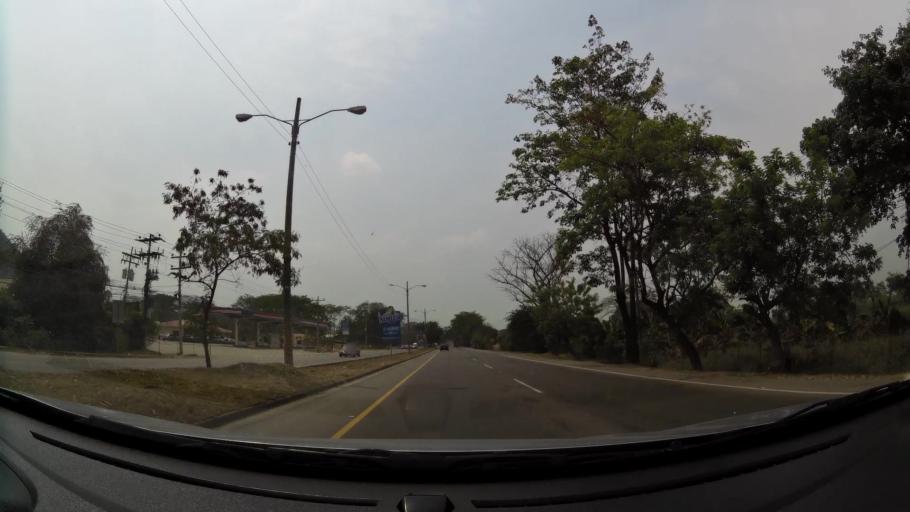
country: HN
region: Cortes
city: Nuevo Chamelecon
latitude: 15.3935
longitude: -87.9937
